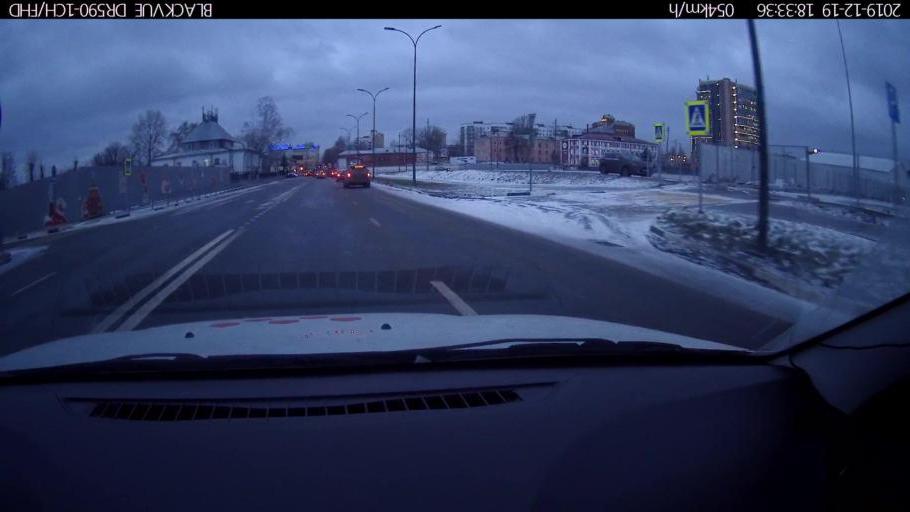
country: RU
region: Nizjnij Novgorod
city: Nizhniy Novgorod
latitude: 56.3331
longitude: 43.9672
